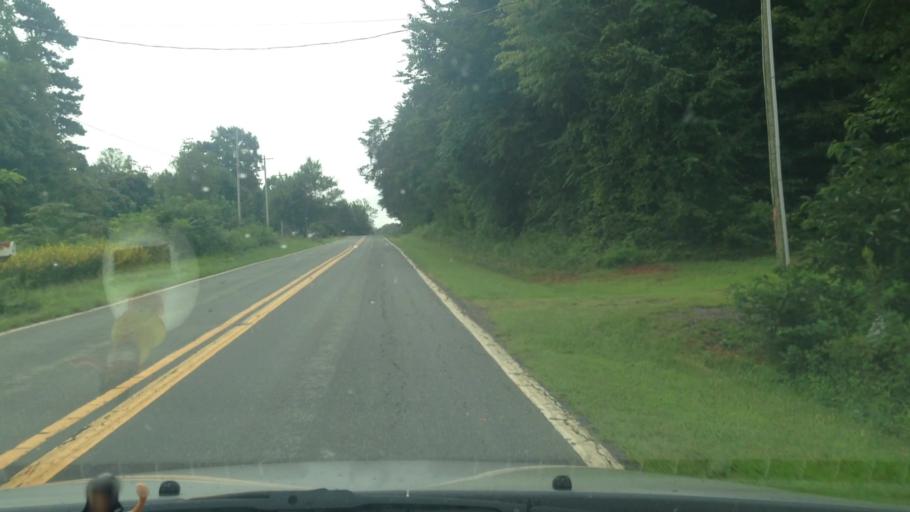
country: US
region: North Carolina
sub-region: Stokes County
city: Danbury
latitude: 36.3883
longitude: -80.1359
